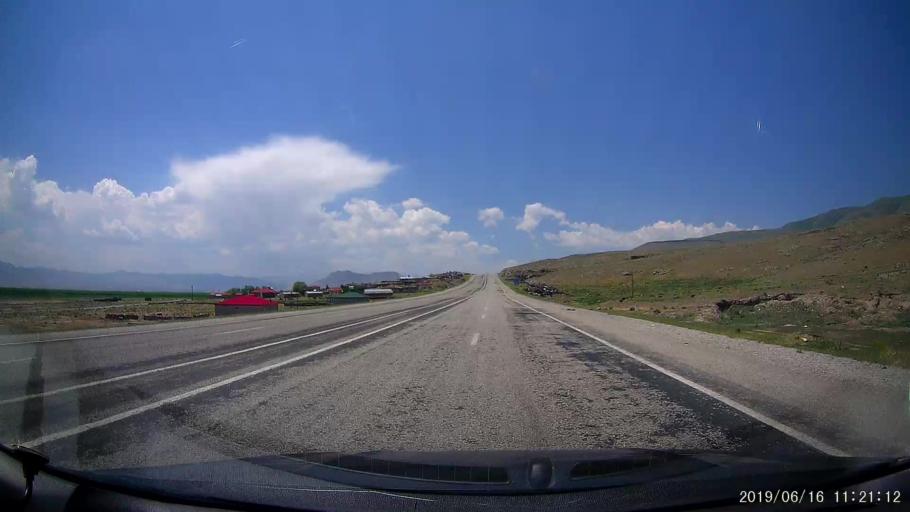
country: TR
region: Agri
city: Dogubayazit
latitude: 39.6948
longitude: 44.0749
